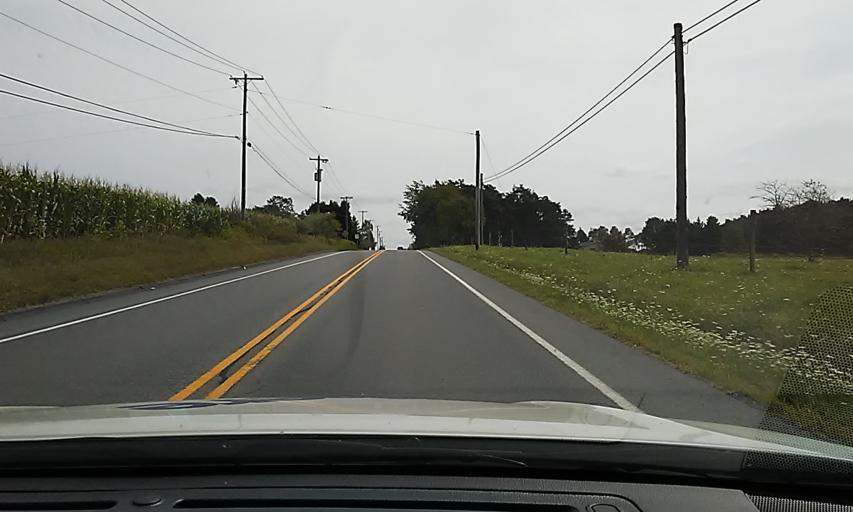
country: US
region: Pennsylvania
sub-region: Elk County
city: Saint Marys
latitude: 41.3617
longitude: -78.5762
